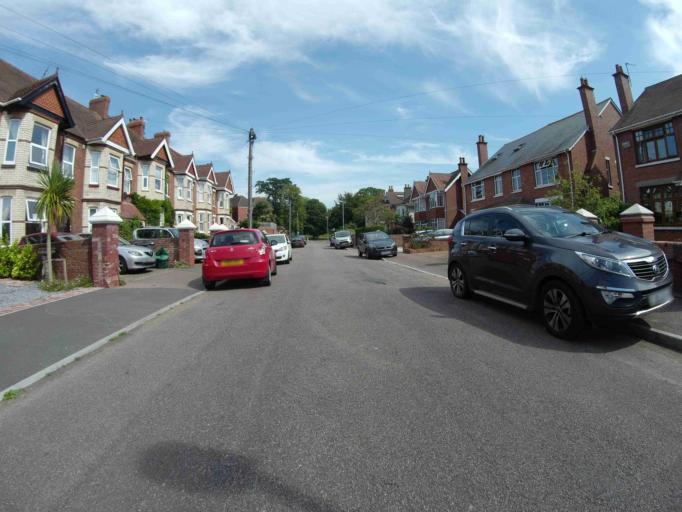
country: GB
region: England
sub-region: Devon
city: Exmouth
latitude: 50.6263
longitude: -3.4082
